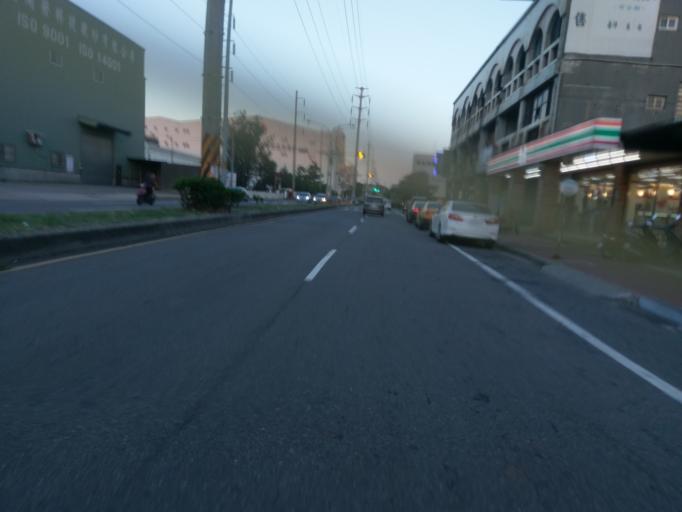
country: TW
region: Taiwan
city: Taoyuan City
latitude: 25.0549
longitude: 121.1248
